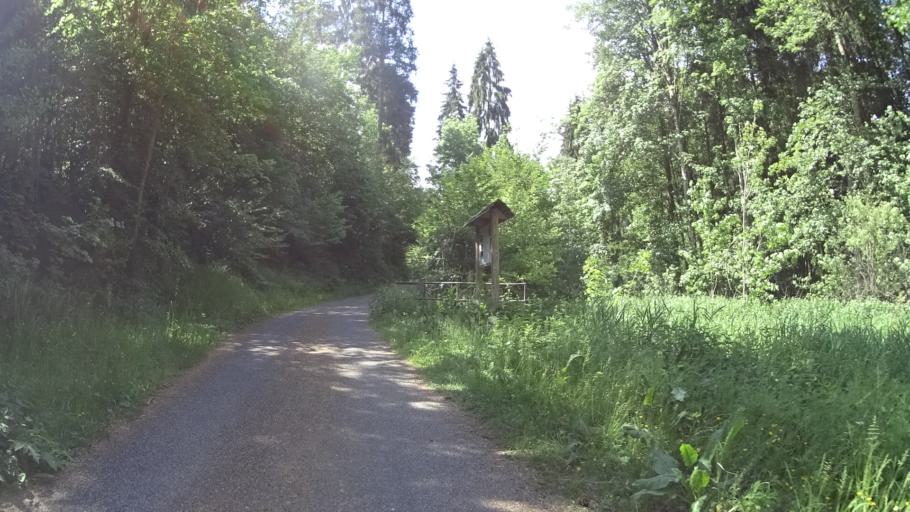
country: DE
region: Baden-Wuerttemberg
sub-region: Karlsruhe Region
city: Hopfingen
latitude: 49.6396
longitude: 9.4374
